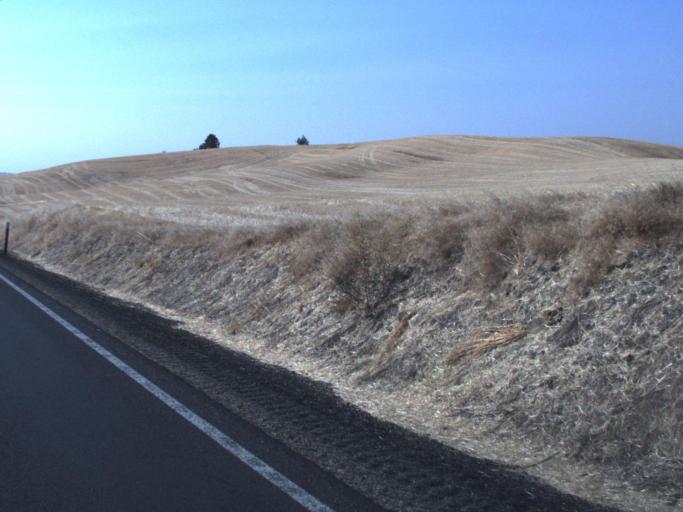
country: US
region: Washington
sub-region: Whitman County
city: Colfax
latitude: 47.1429
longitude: -117.2376
